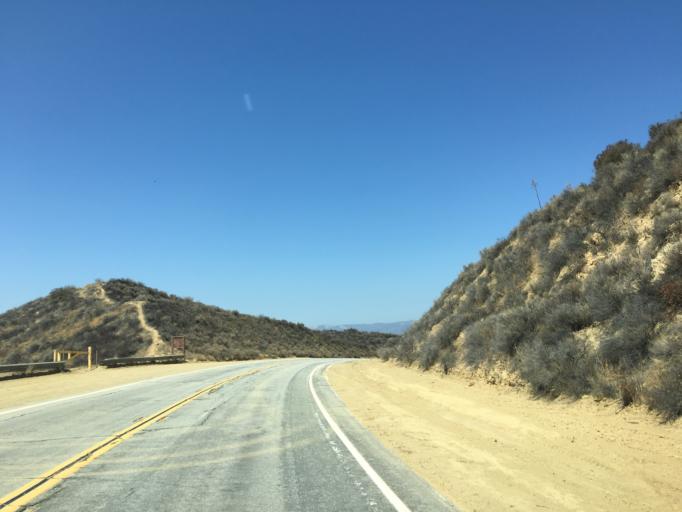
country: US
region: California
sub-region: Los Angeles County
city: Castaic
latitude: 34.5166
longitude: -118.5828
